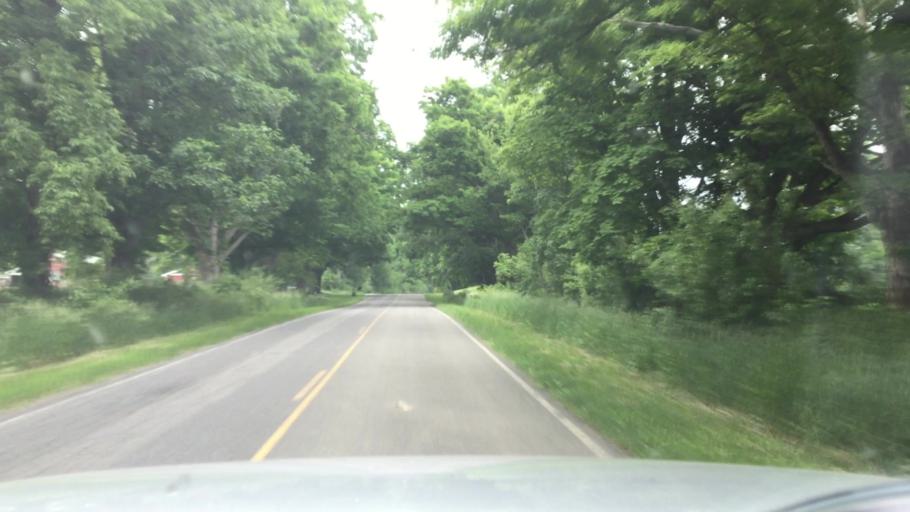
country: US
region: Michigan
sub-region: Shiawassee County
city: Durand
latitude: 42.7843
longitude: -84.0014
